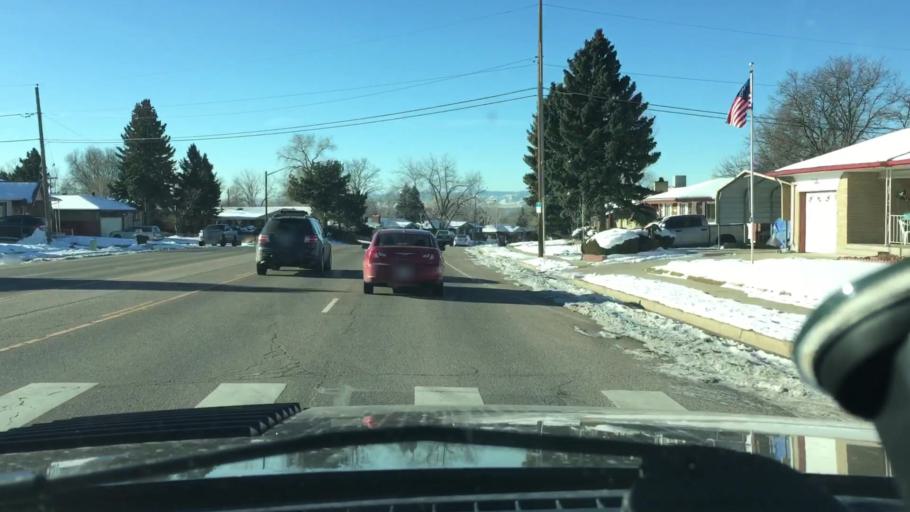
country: US
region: Colorado
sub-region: Adams County
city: Sherrelwood
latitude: 39.8437
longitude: -104.9985
